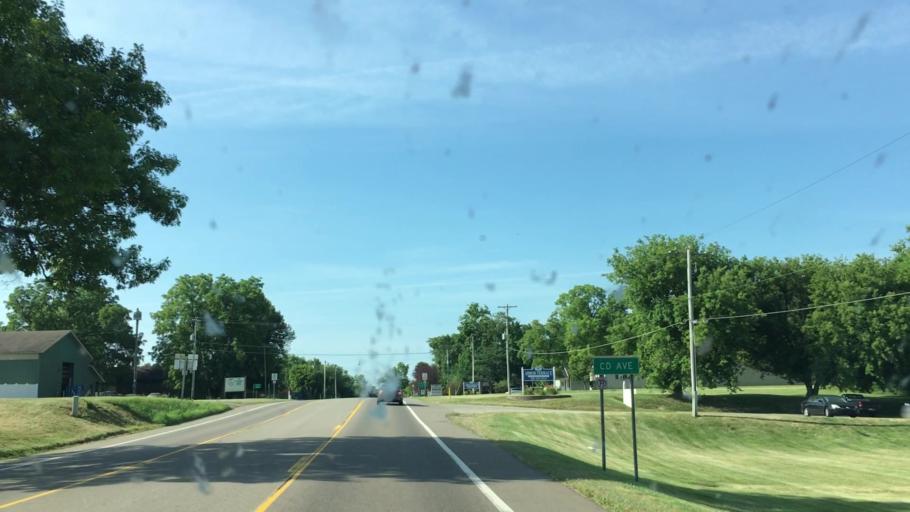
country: US
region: Michigan
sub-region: Kalamazoo County
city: South Gull Lake
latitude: 42.3847
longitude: -85.4553
